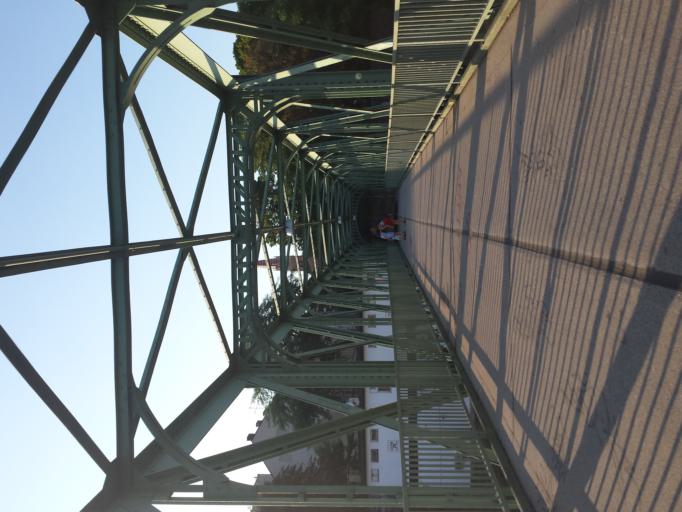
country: AT
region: Vienna
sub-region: Wien Stadt
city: Vienna
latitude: 48.1942
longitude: 16.3258
